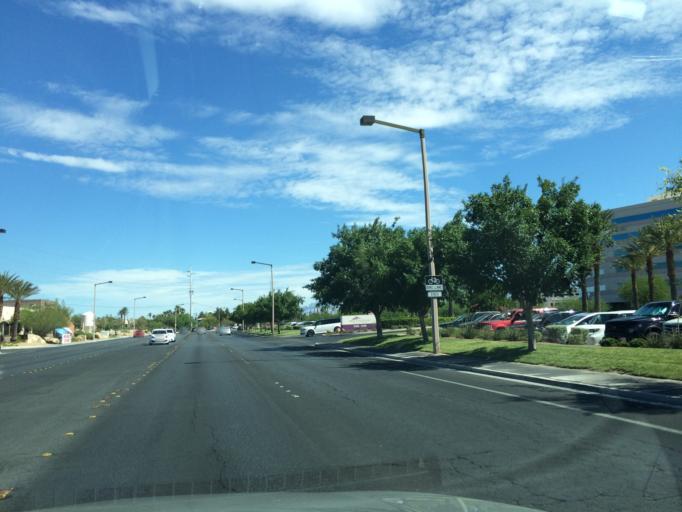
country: US
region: Nevada
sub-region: Clark County
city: Spring Valley
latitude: 36.2151
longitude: -115.2505
